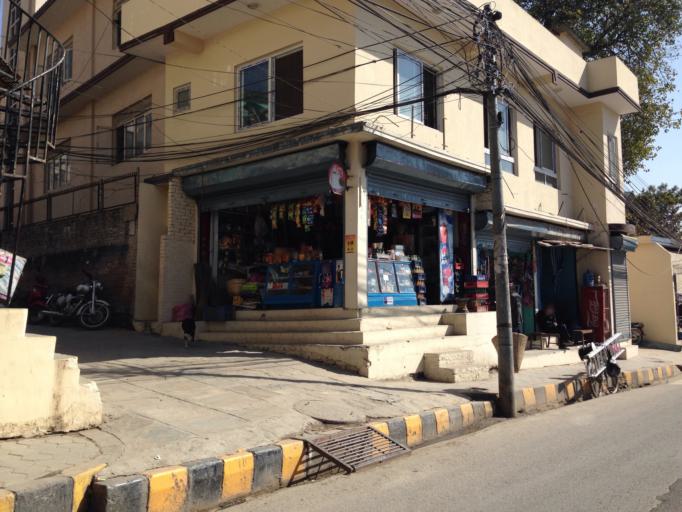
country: NP
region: Central Region
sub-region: Bagmati Zone
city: Kathmandu
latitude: 27.7253
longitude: 85.3307
